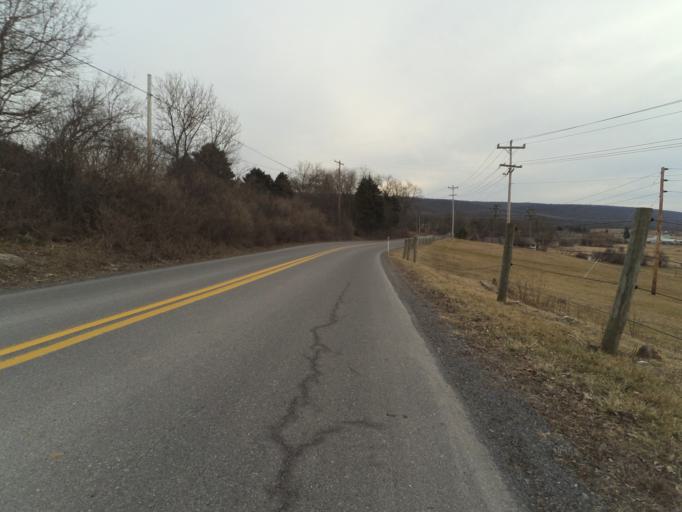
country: US
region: Pennsylvania
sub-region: Centre County
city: State College
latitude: 40.7655
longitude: -77.8416
